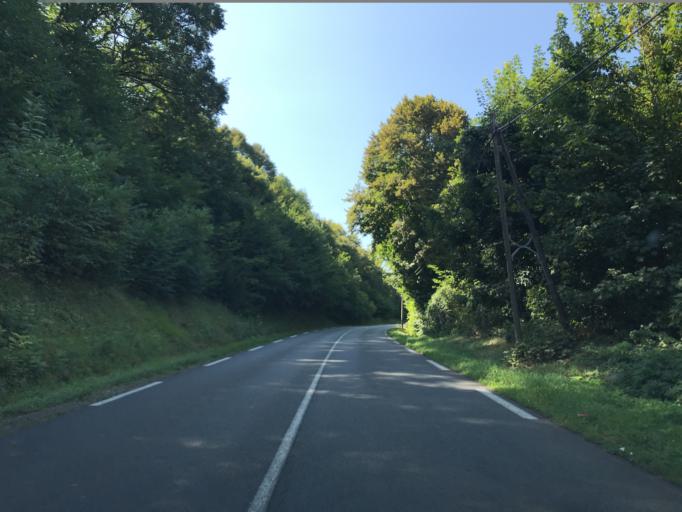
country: FR
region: Haute-Normandie
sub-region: Departement de l'Eure
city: Houlbec-Cocherel
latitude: 49.0620
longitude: 1.2789
